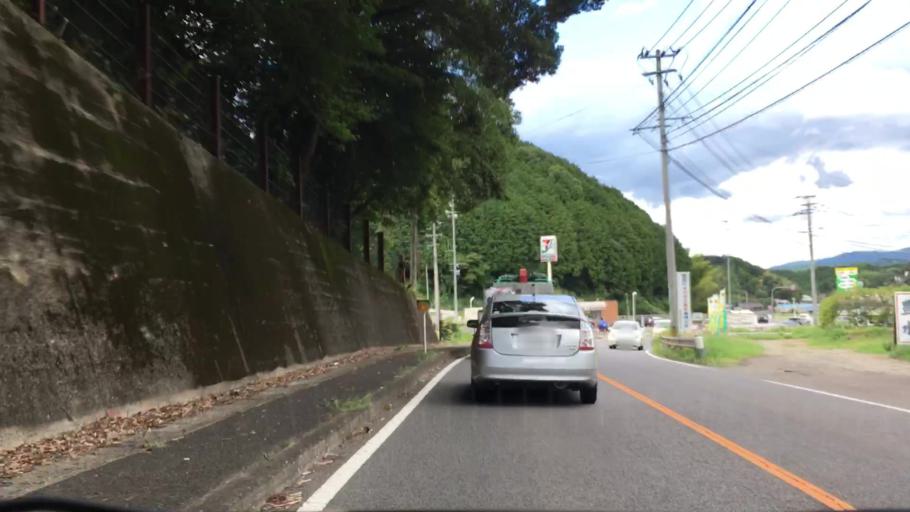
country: JP
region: Saga Prefecture
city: Imaricho-ko
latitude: 33.2924
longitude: 129.9095
